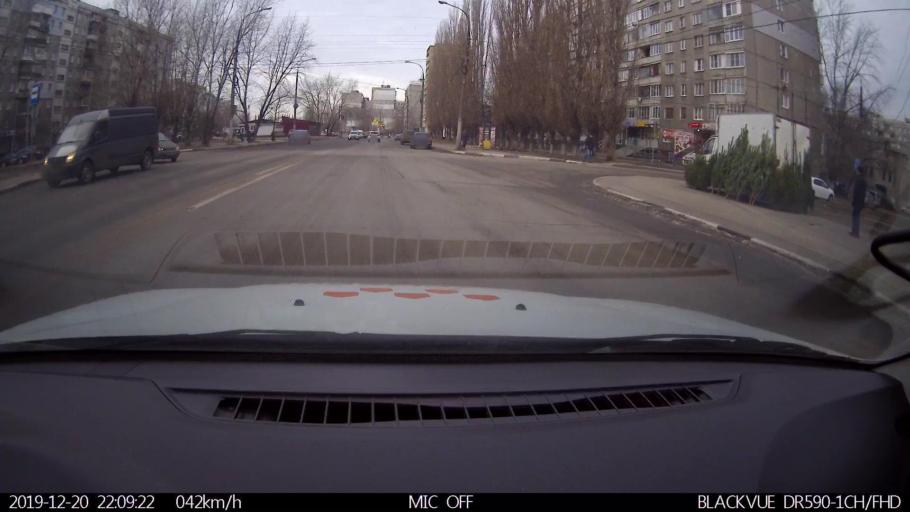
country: RU
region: Nizjnij Novgorod
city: Nizhniy Novgorod
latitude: 56.3438
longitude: 43.9300
